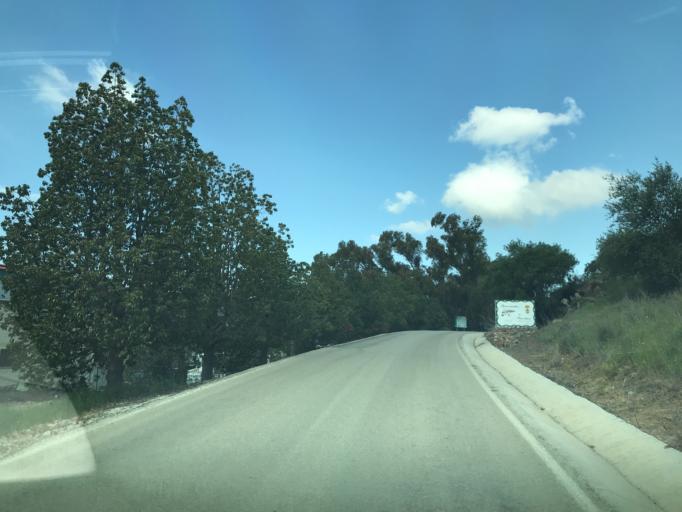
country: ES
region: Andalusia
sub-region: Provincia de Malaga
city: Periana
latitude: 36.9247
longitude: -4.1803
